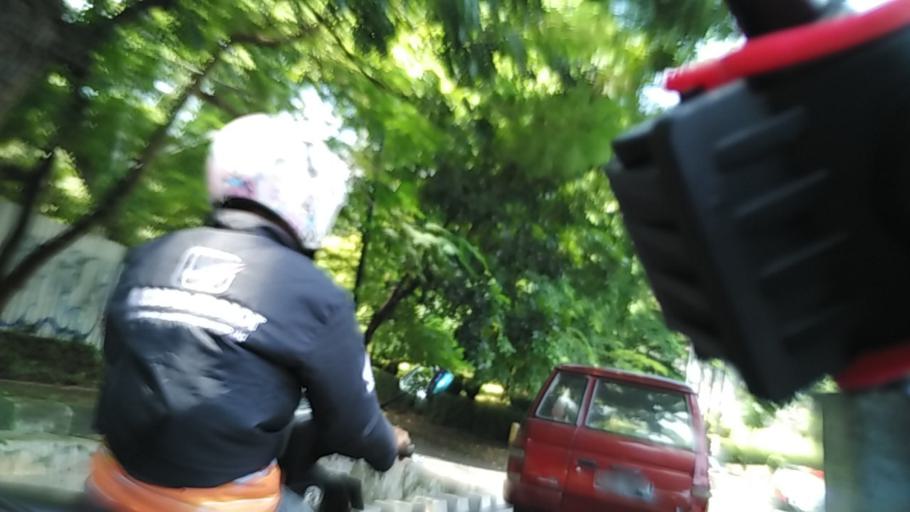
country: ID
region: Central Java
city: Semarang
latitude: -7.0044
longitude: 110.4083
